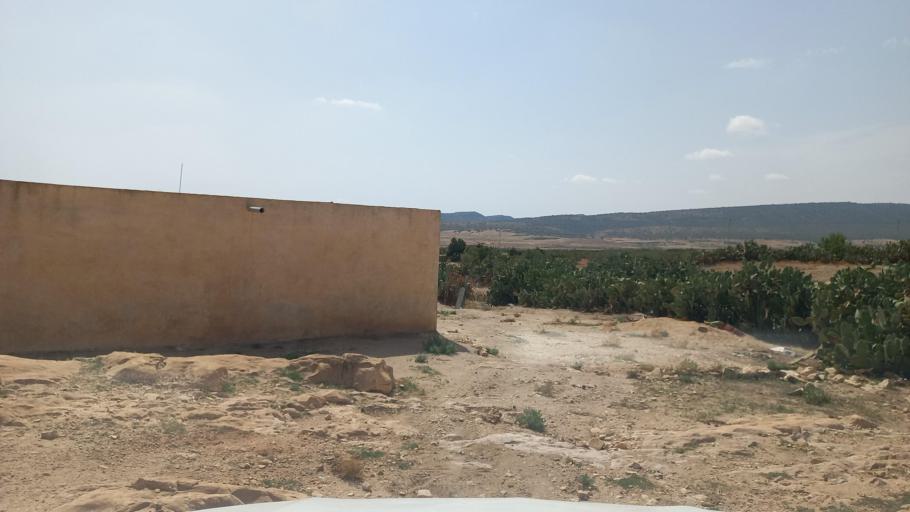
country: TN
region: Al Qasrayn
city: Sbiba
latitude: 35.4029
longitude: 8.9699
